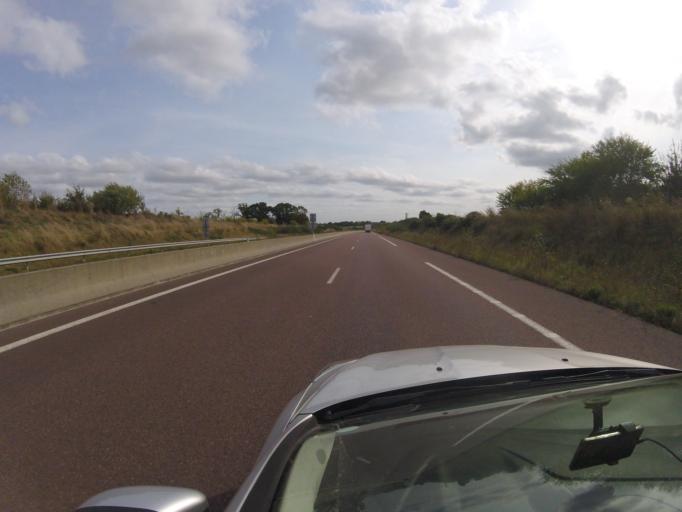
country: FR
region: Lower Normandy
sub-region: Departement de la Manche
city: Saint-Hilaire-Petitville
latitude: 49.2928
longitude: -1.1647
